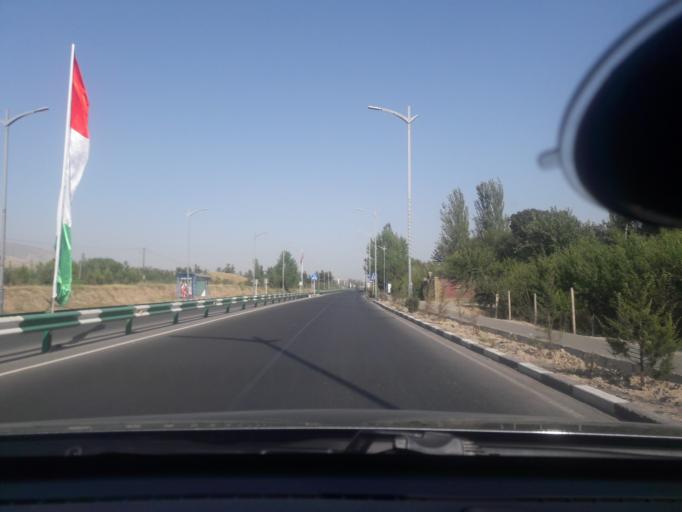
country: TJ
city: Shahrinav
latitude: 38.5763
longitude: 68.3409
